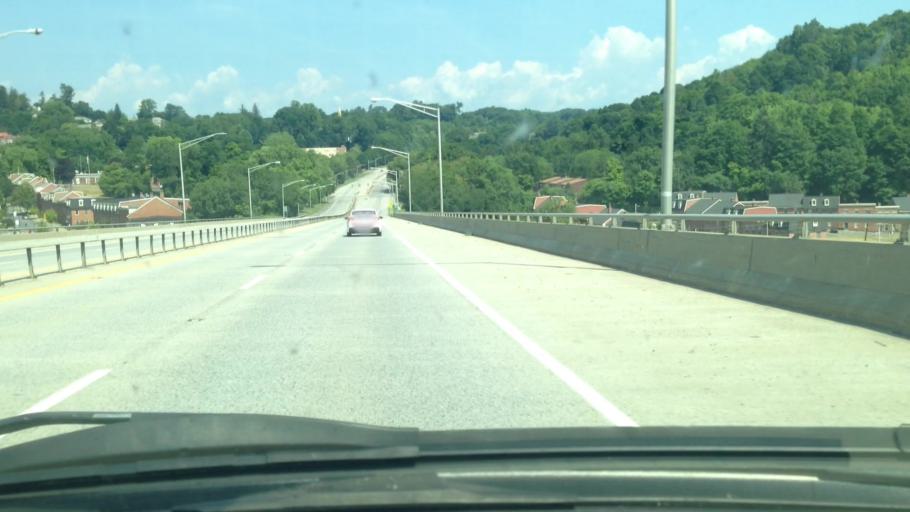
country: US
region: New York
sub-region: Ulster County
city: Port Ewen
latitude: 41.9173
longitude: -73.9813
